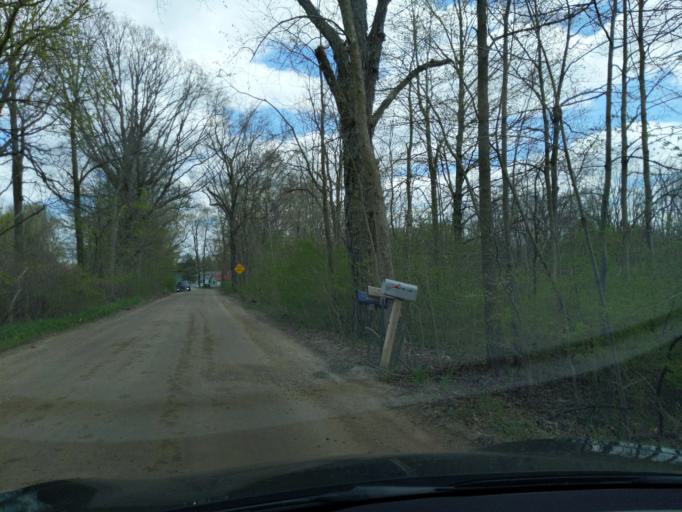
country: US
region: Michigan
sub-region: Eaton County
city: Dimondale
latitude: 42.6263
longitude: -84.6055
